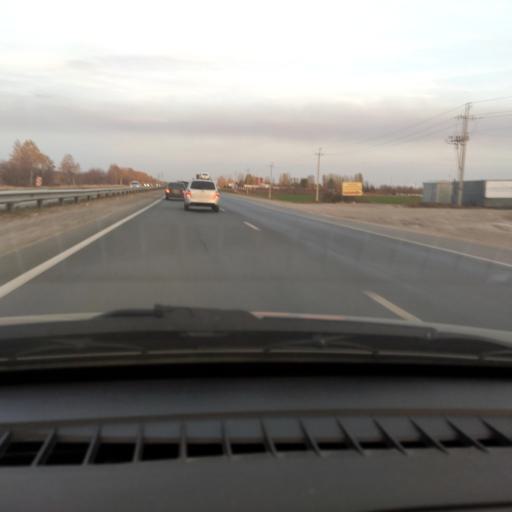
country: RU
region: Samara
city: Tol'yatti
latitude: 53.5781
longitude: 49.4172
